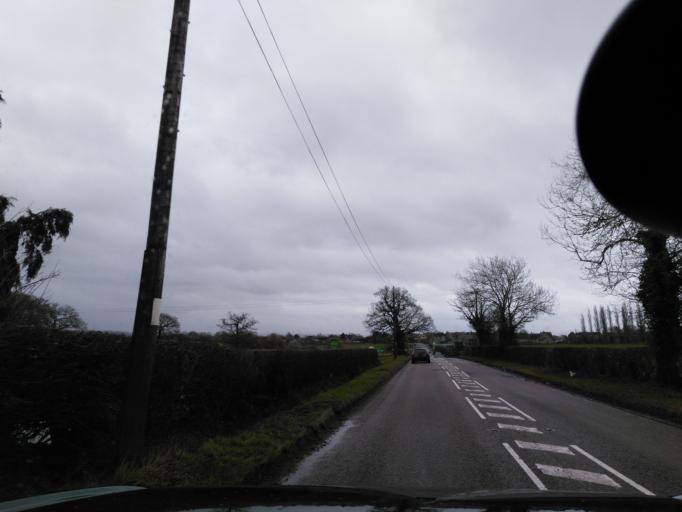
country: GB
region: England
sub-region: Wiltshire
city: Atworth
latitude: 51.3958
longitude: -2.2045
